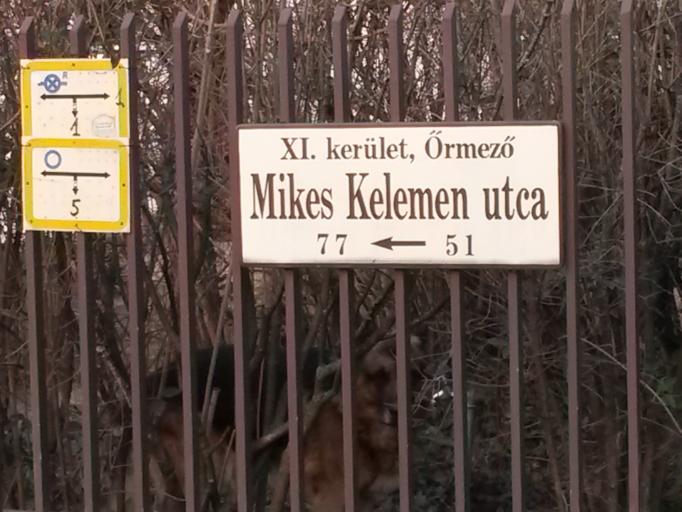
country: HU
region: Budapest
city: Budapest XI. keruelet
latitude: 47.4588
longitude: 19.0133
